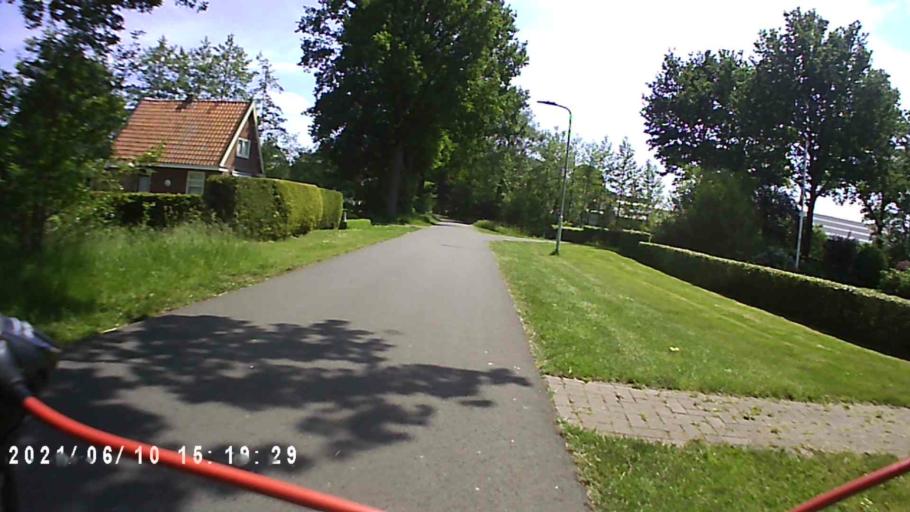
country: NL
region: Friesland
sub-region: Gemeente Achtkarspelen
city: Surhuisterveen
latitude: 53.1948
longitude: 6.1723
